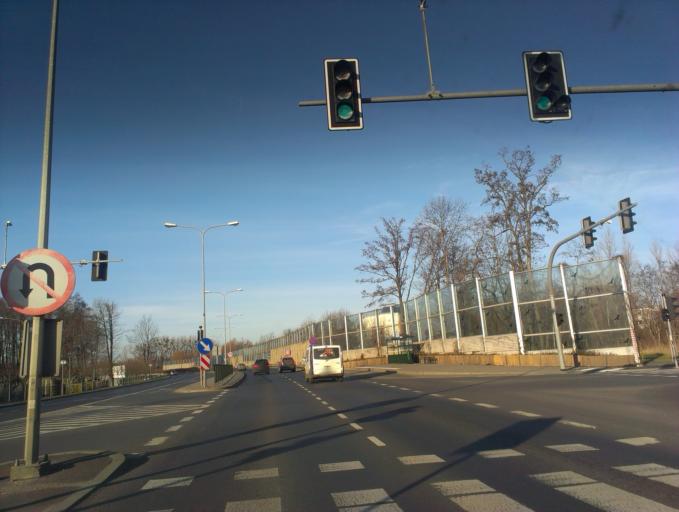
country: PL
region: Greater Poland Voivodeship
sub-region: Poznan
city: Poznan
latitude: 52.4377
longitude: 16.9533
